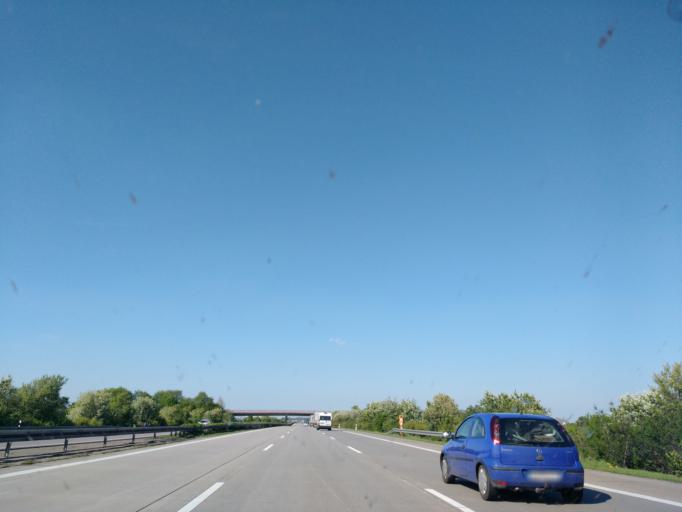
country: DE
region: Saxony
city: Grosslehna
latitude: 51.3108
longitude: 12.1587
